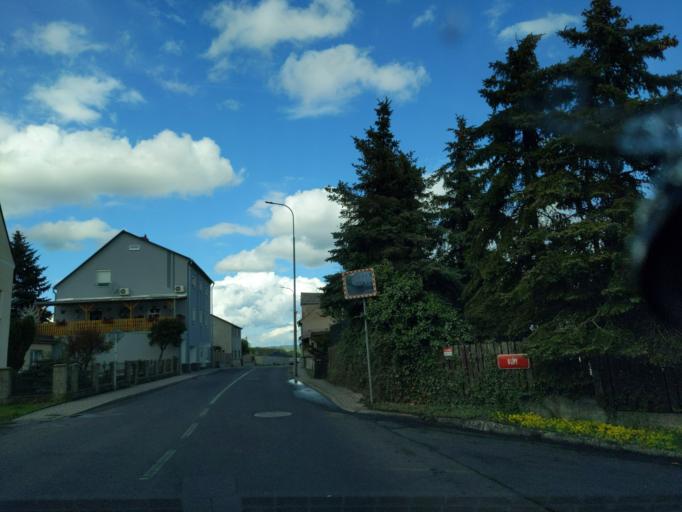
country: CZ
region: Ustecky
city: Krupka
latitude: 50.6872
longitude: 13.8991
